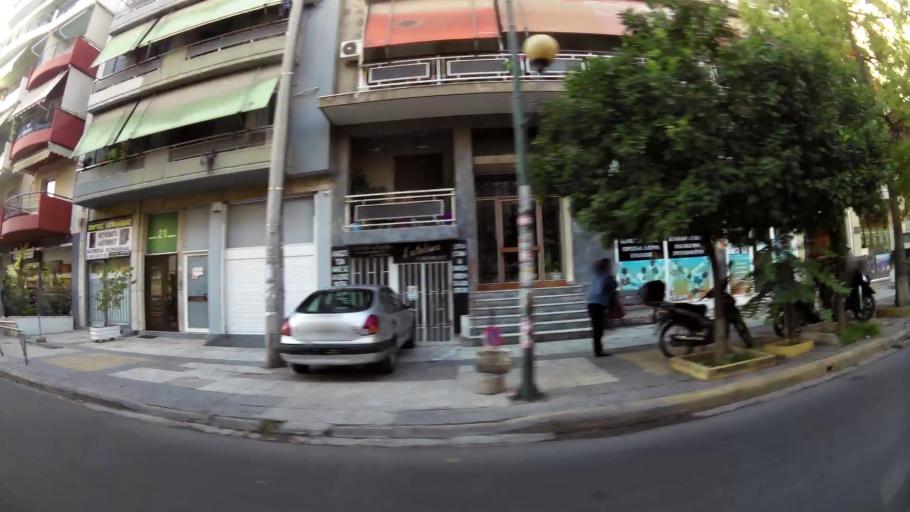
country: GR
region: Attica
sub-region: Nomos Piraios
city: Agios Ioannis Rentis
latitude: 37.9751
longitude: 23.6609
